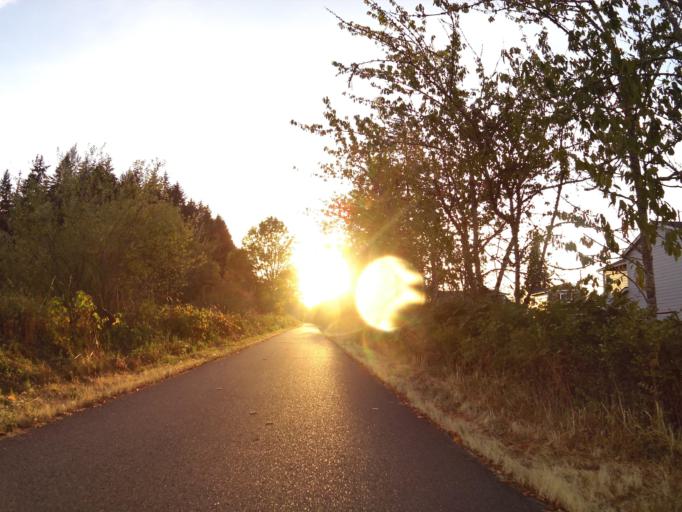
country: US
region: Washington
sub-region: Thurston County
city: Tenino
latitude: 46.8571
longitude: -122.8296
